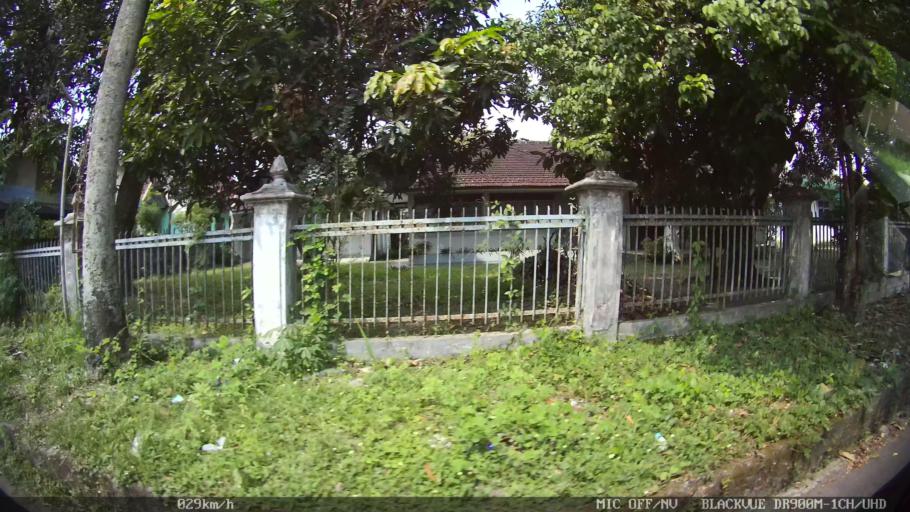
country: ID
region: Daerah Istimewa Yogyakarta
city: Depok
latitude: -7.7996
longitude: 110.4077
